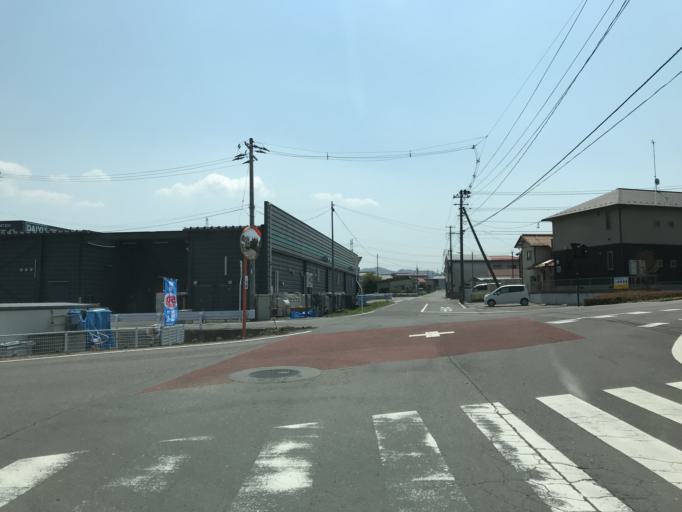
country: JP
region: Fukushima
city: Ishikawa
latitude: 37.0845
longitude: 140.4171
